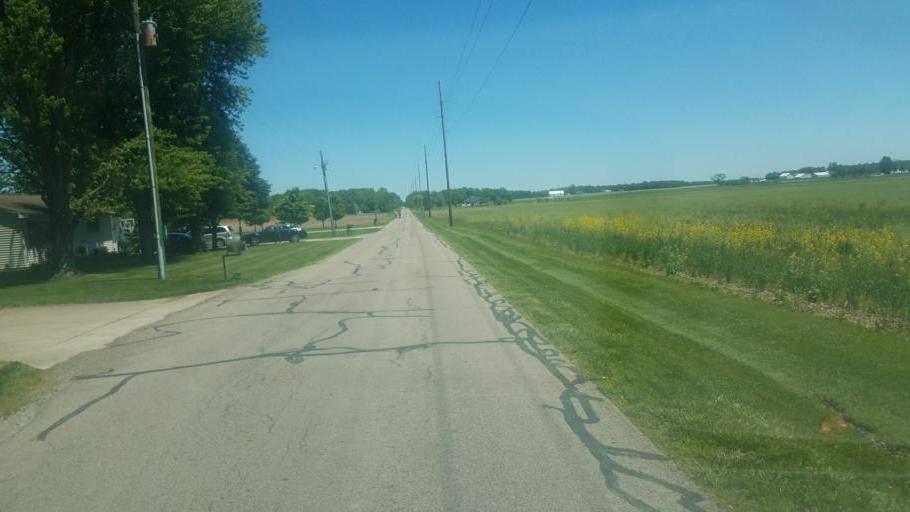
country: US
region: Ohio
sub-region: Darke County
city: Versailles
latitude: 40.2264
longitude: -84.4090
